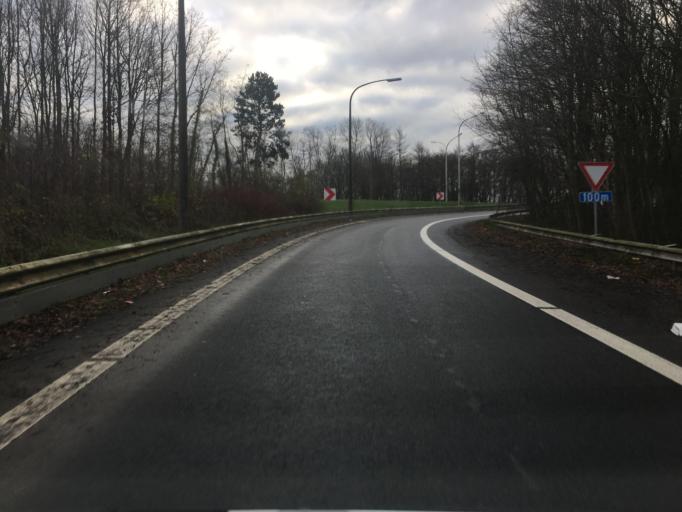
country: BE
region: Wallonia
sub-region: Province du Hainaut
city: Manage
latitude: 50.5076
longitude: 4.2119
